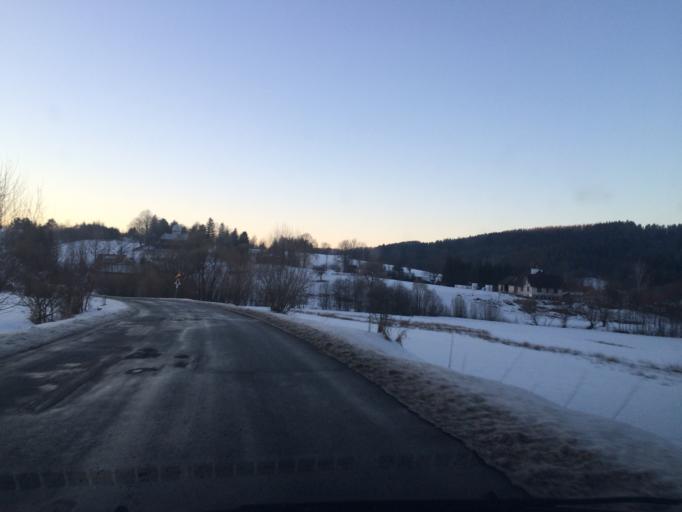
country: PL
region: Subcarpathian Voivodeship
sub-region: Powiat bieszczadzki
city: Ustrzyki Dolne
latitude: 49.3924
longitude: 22.6264
